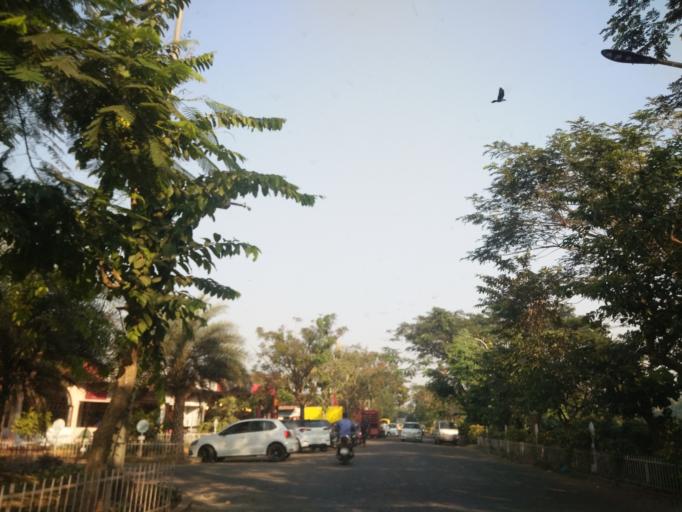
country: IN
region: Goa
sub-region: South Goa
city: Madgaon
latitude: 15.2852
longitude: 73.9592
